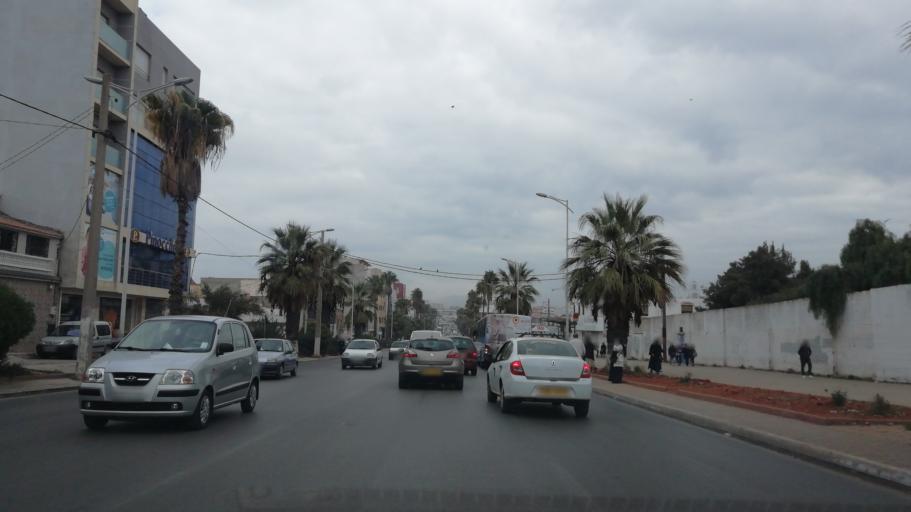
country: DZ
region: Oran
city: Oran
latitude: 35.6921
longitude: -0.6188
